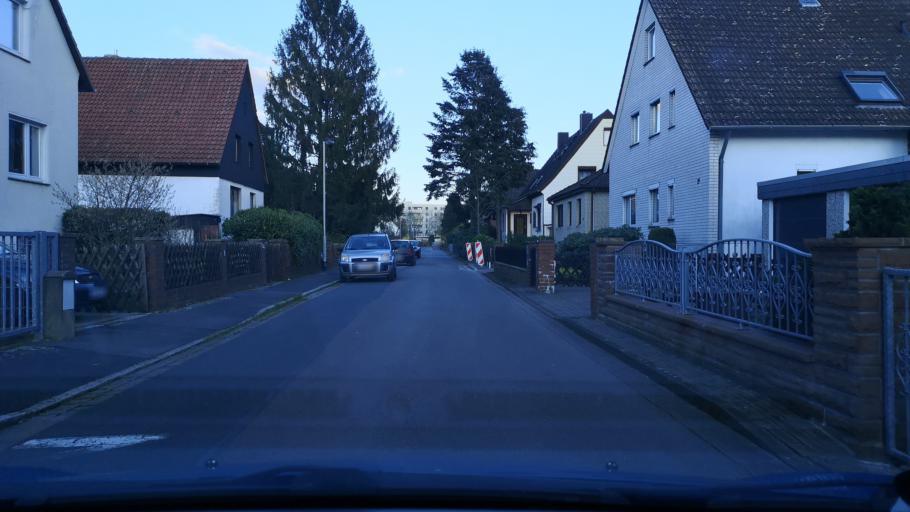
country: DE
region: Lower Saxony
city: Langenhagen
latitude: 52.4131
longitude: 9.7694
